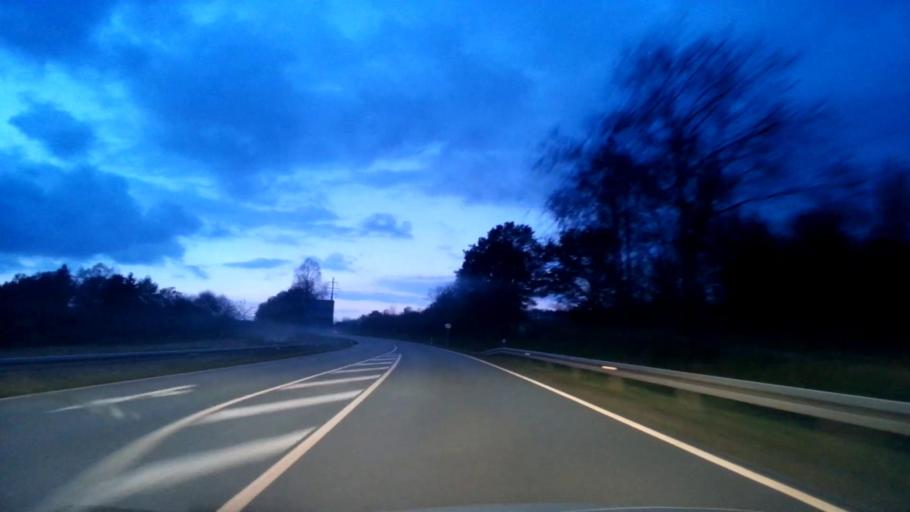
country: DE
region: Bavaria
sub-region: Upper Franconia
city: Kirchenpingarten
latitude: 49.9425
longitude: 11.7387
